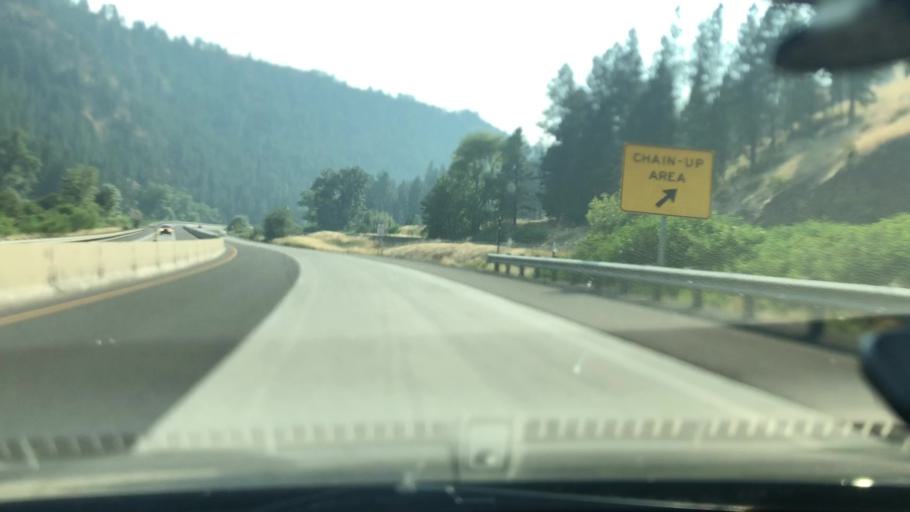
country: US
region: Oregon
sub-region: Union County
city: La Grande
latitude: 45.3523
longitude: -118.1968
